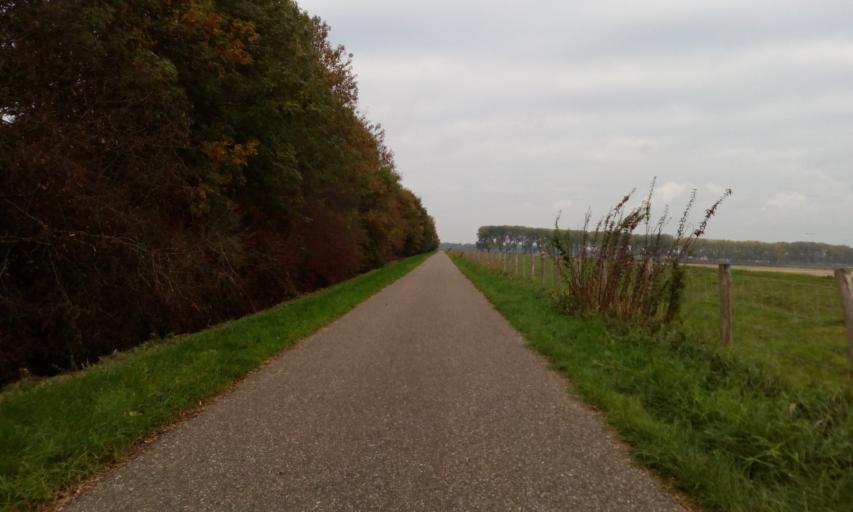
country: NL
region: South Holland
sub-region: Gemeente Binnenmaas
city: Heinenoord
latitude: 51.8386
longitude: 4.4574
